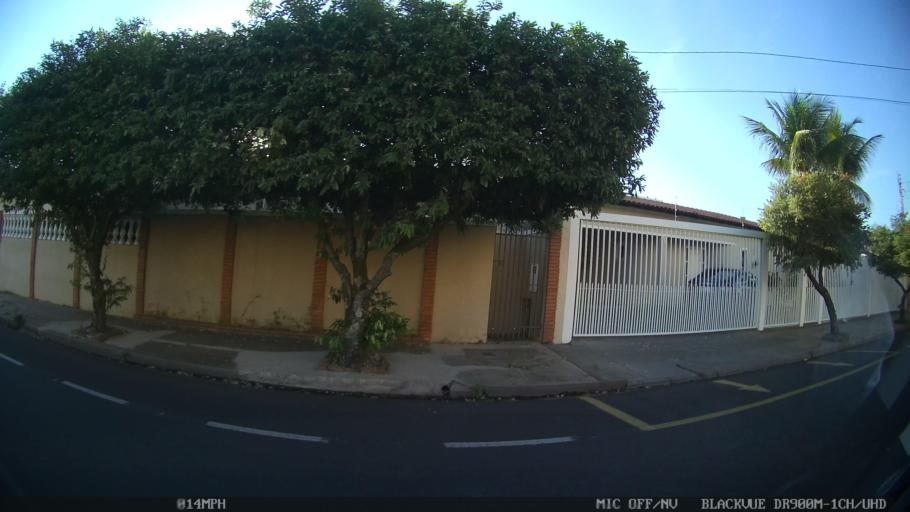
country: BR
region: Sao Paulo
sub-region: Sao Jose Do Rio Preto
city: Sao Jose do Rio Preto
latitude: -20.7973
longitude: -49.3612
